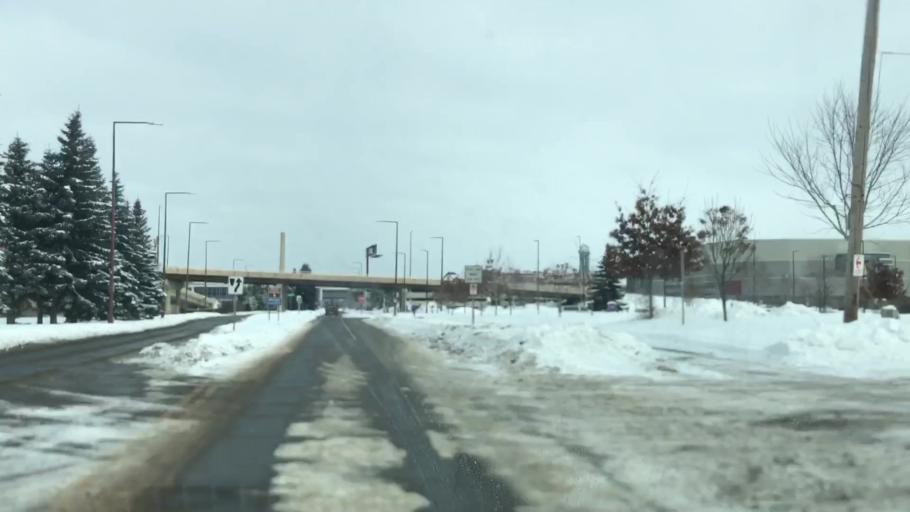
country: US
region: Minnesota
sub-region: Saint Louis County
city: Duluth
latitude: 46.7797
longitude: -92.1034
